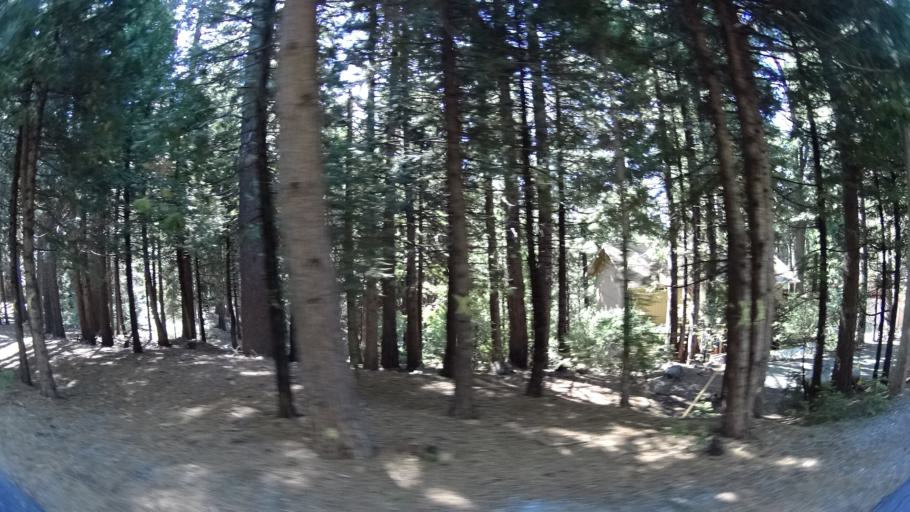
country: US
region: California
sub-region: Calaveras County
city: Arnold
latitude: 38.2927
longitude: -120.2680
